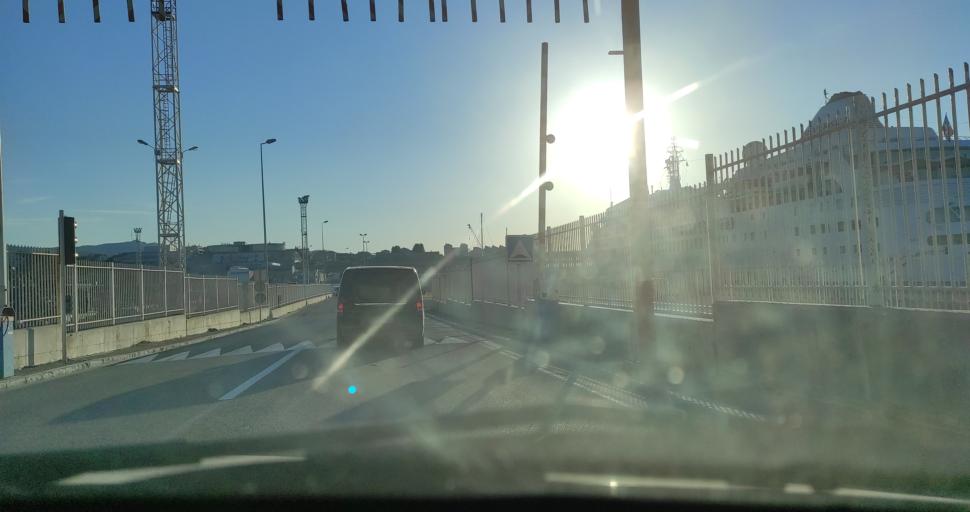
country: FR
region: Provence-Alpes-Cote d'Azur
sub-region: Departement des Bouches-du-Rhone
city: Marseille 03
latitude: 43.3239
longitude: 5.3525
